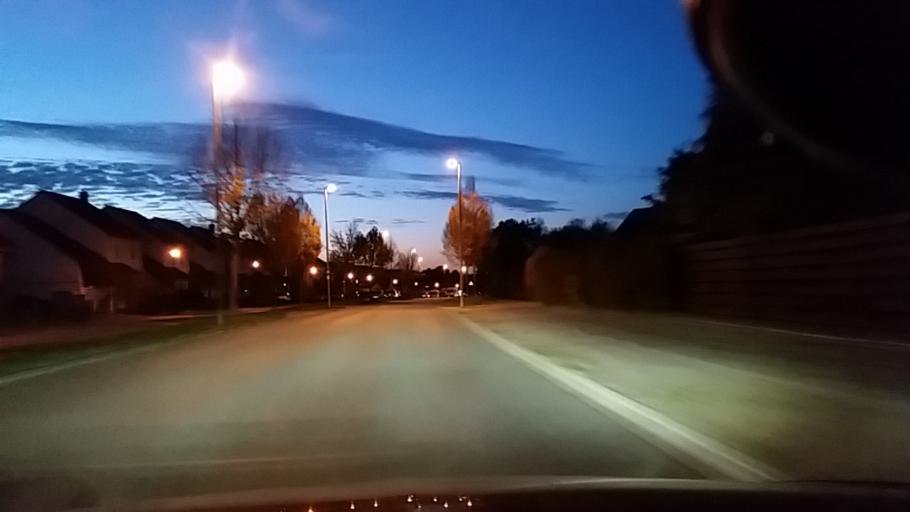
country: DE
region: Lower Saxony
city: Wolfsburg
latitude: 52.4511
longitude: 10.7849
